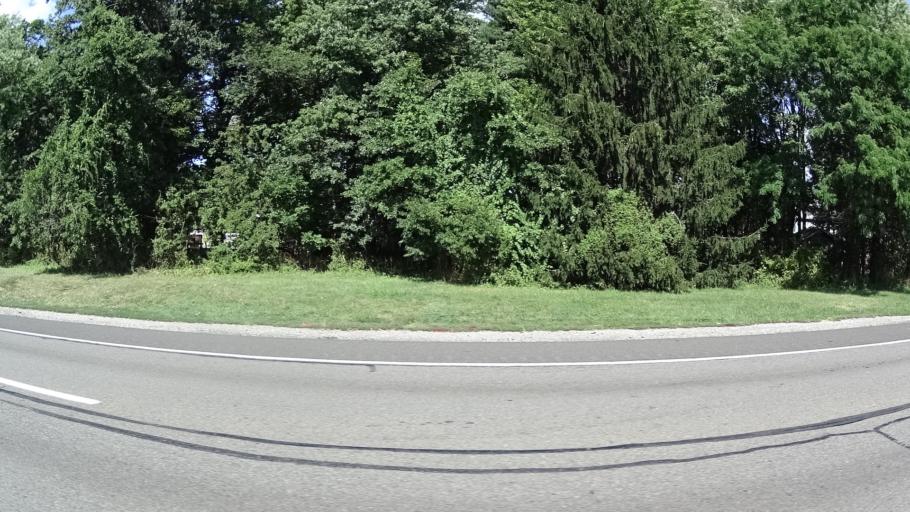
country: US
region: New Jersey
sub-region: Union County
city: Kenilworth
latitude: 40.6684
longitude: -74.2844
